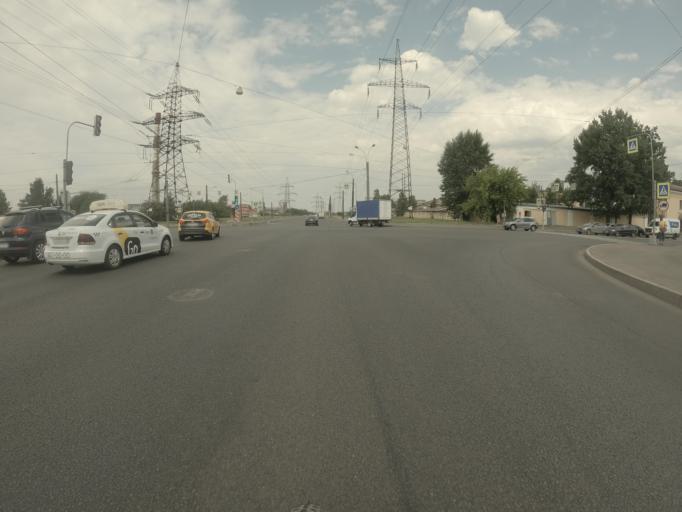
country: RU
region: St.-Petersburg
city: Krasnogvargeisky
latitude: 59.9619
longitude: 30.4609
